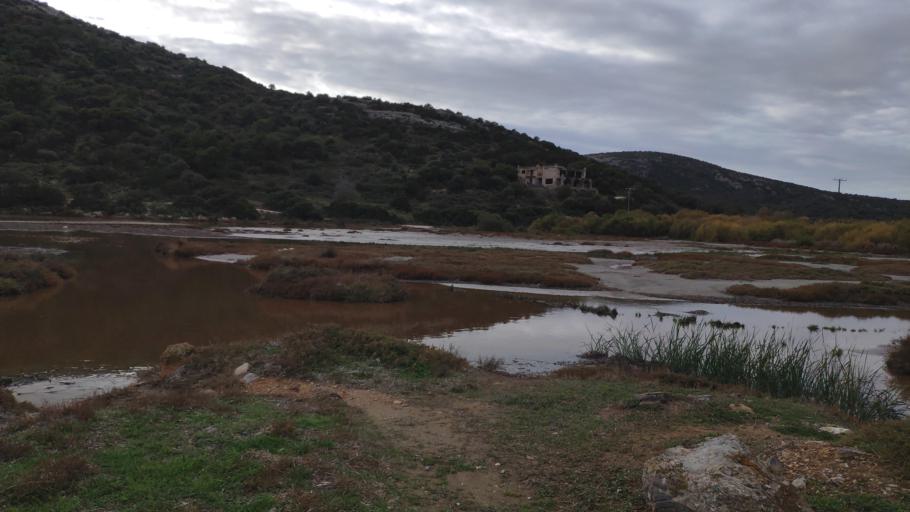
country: GR
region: Attica
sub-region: Nomarchia Anatolikis Attikis
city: Limin Mesoyaias
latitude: 37.9263
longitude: 24.0017
